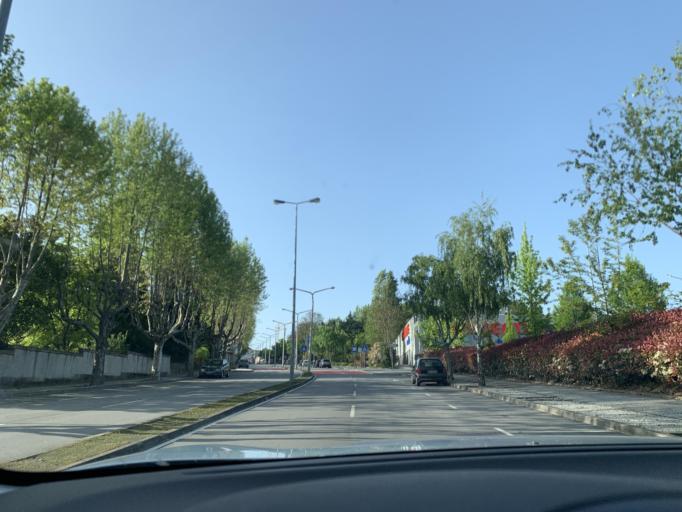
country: PT
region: Viseu
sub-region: Mangualde
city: Mangualde
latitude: 40.6014
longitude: -7.7617
